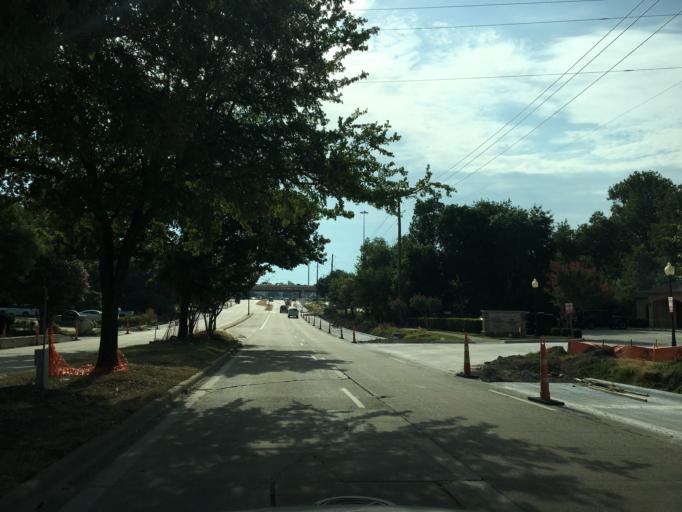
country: US
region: Texas
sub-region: Collin County
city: McKinney
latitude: 33.1985
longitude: -96.6425
